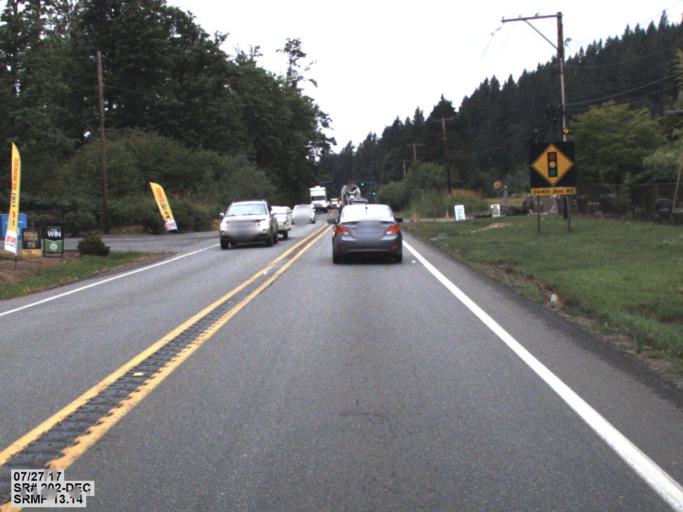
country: US
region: Washington
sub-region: King County
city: Ames Lake
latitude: 47.6387
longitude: -122.0079
